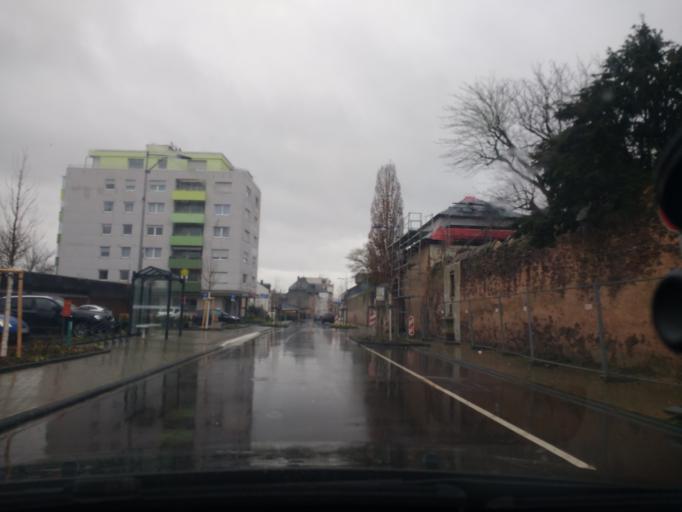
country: DE
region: Rheinland-Pfalz
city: Konz
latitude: 49.7110
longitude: 6.5920
